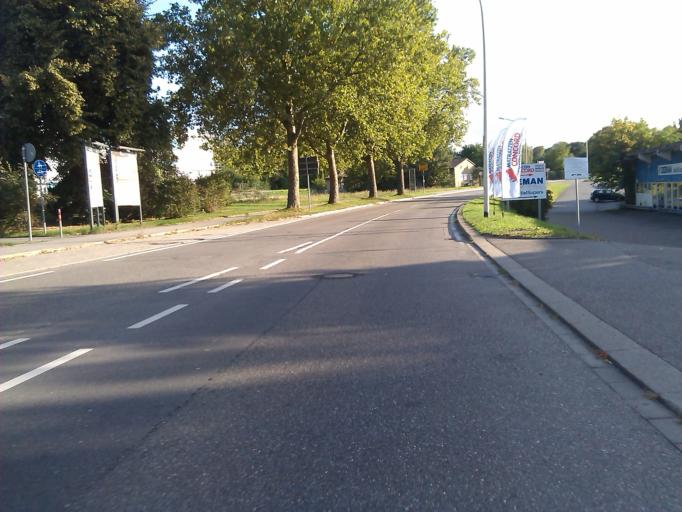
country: DE
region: Baden-Wuerttemberg
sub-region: Regierungsbezirk Stuttgart
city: Flein
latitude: 49.1201
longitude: 9.2163
